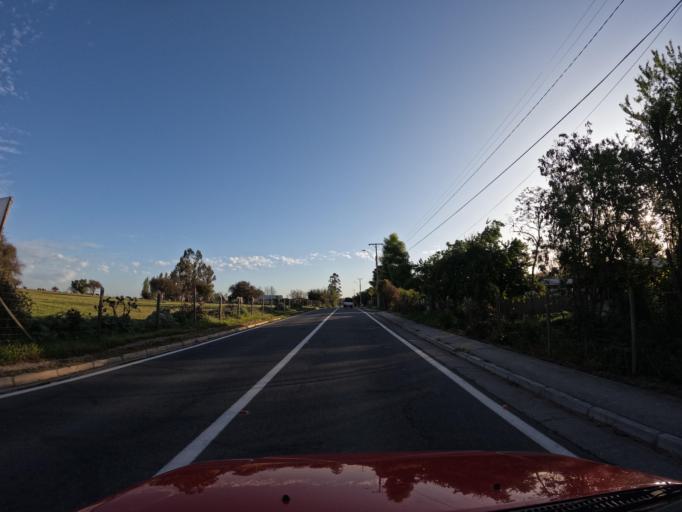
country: CL
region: O'Higgins
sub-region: Provincia de Colchagua
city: Santa Cruz
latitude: -34.2217
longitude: -71.7217
